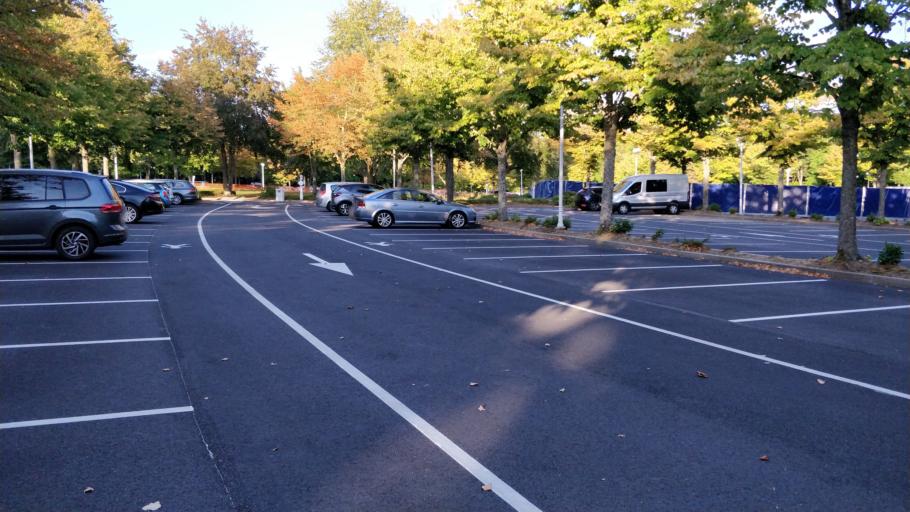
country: FR
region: Ile-de-France
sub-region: Departement de Seine-et-Marne
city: Serris
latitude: 48.8642
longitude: 2.7887
